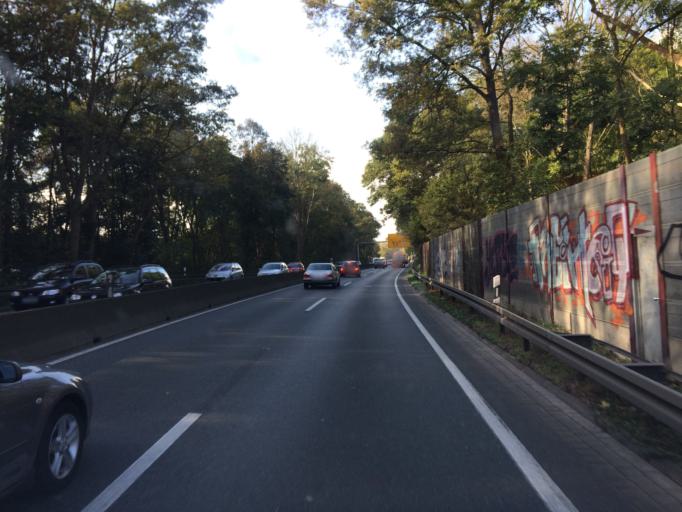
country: DE
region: Lower Saxony
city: Hemmingen
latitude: 52.3364
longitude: 9.7268
